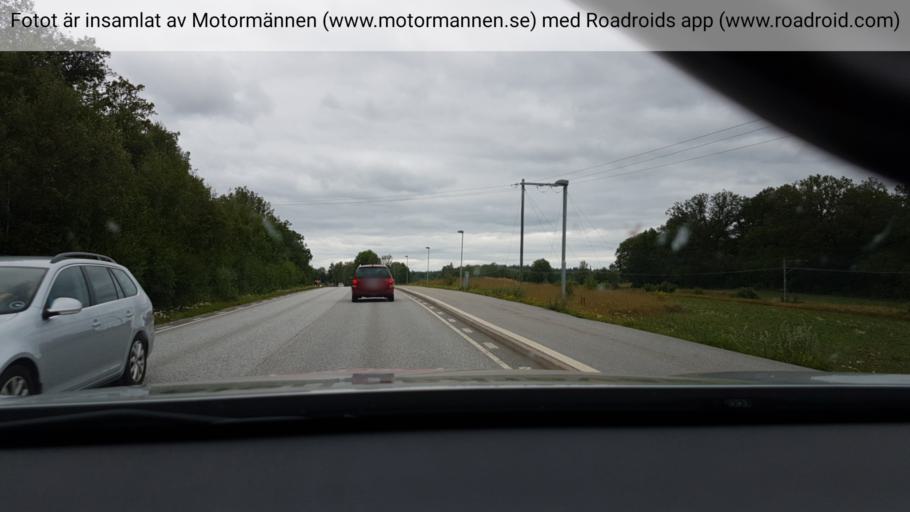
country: SE
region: Stockholm
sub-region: Nynashamns Kommun
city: Nynashamn
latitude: 58.9373
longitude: 17.9164
